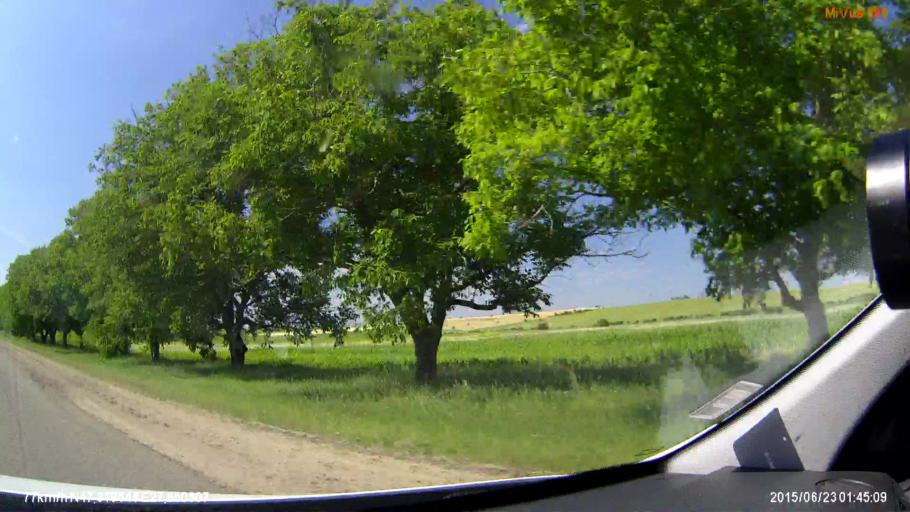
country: RO
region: Iasi
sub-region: Comuna Victoria
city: Victoria
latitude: 47.3195
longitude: 27.6506
